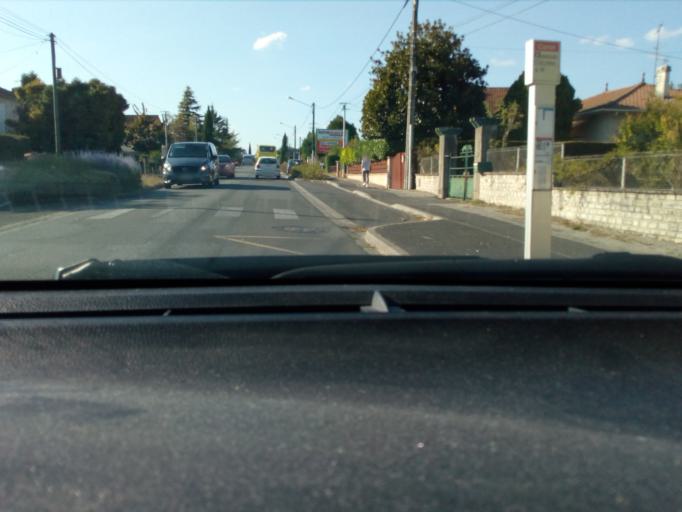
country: FR
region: Poitou-Charentes
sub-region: Departement de la Charente
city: Saint-Yrieix-sur-Charente
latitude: 45.6752
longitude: 0.1232
